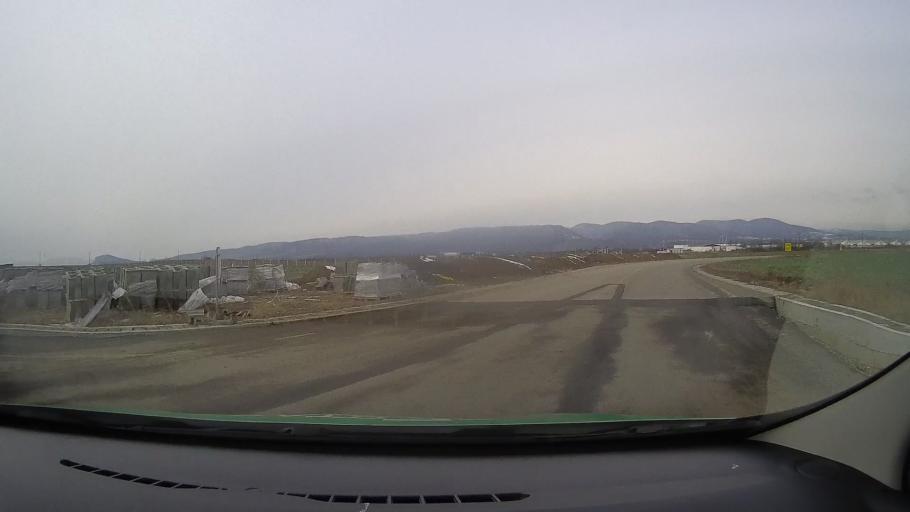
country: RO
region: Hunedoara
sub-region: Comuna Turdas
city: Turdas
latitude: 45.8409
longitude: 23.1363
